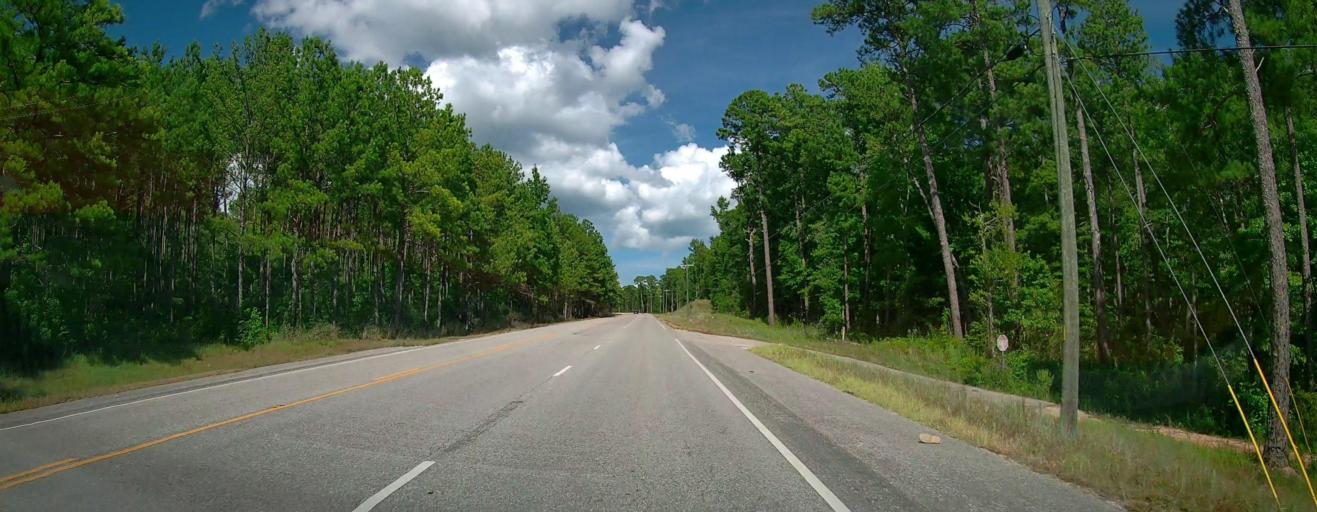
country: US
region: Alabama
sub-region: Macon County
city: Tuskegee
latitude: 32.4468
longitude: -85.6401
